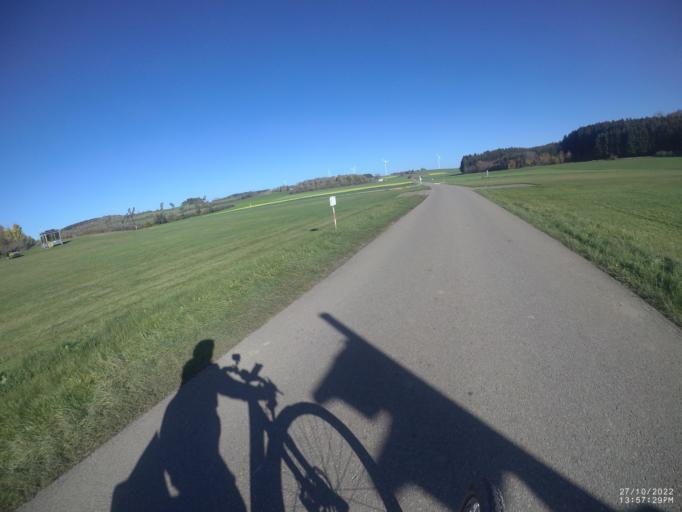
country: DE
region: Baden-Wuerttemberg
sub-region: Regierungsbezirk Stuttgart
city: Bad Ditzenbach
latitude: 48.5650
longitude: 9.7261
